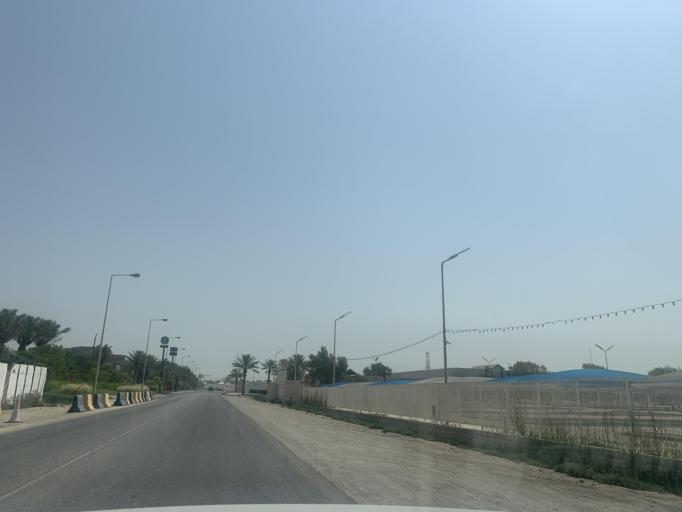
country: BH
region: Central Governorate
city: Madinat Hamad
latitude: 26.1588
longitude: 50.4688
